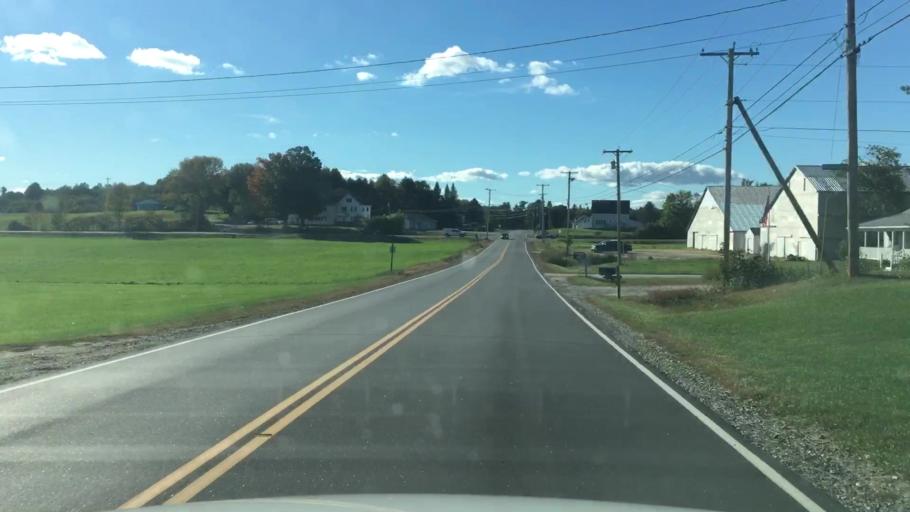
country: US
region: Maine
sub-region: Androscoggin County
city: Sabattus
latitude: 44.0756
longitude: -70.1122
